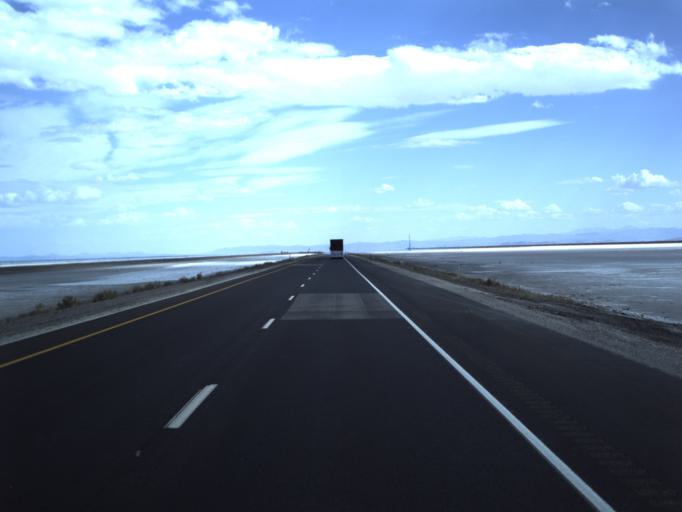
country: US
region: Utah
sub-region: Tooele County
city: Wendover
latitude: 40.7336
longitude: -113.6188
